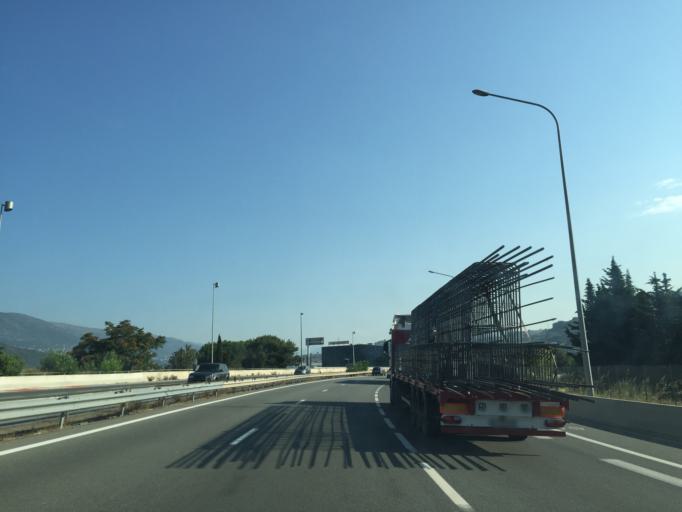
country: FR
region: Provence-Alpes-Cote d'Azur
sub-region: Departement des Alpes-Maritimes
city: Saint-Laurent-du-Var
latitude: 43.7041
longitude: 7.1884
